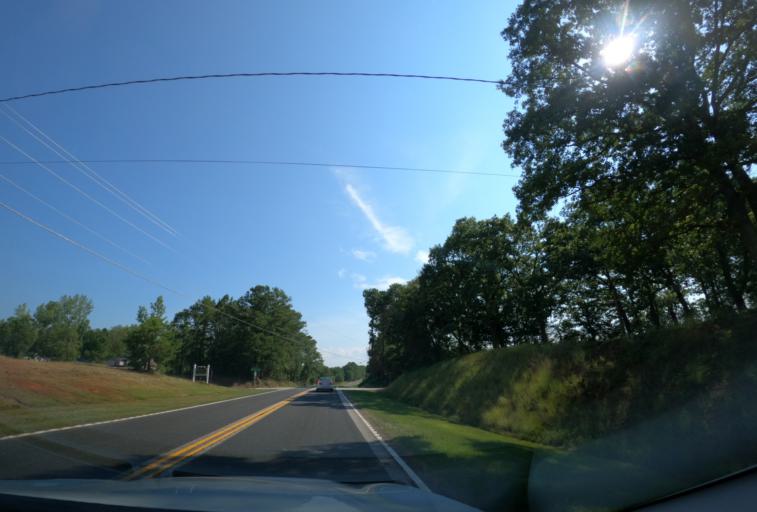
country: US
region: South Carolina
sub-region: Anderson County
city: Belton
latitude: 34.4645
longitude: -82.5380
